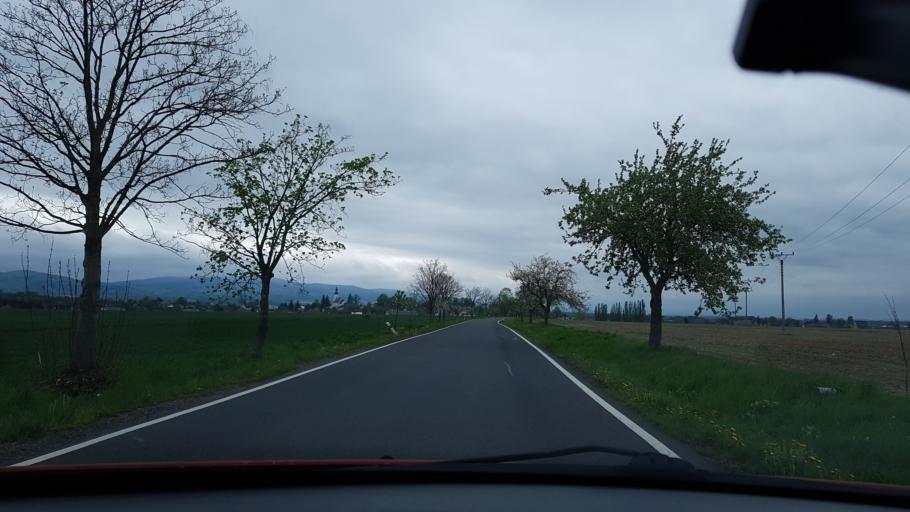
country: CZ
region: Olomoucky
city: Zulova
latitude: 50.3861
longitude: 17.0916
